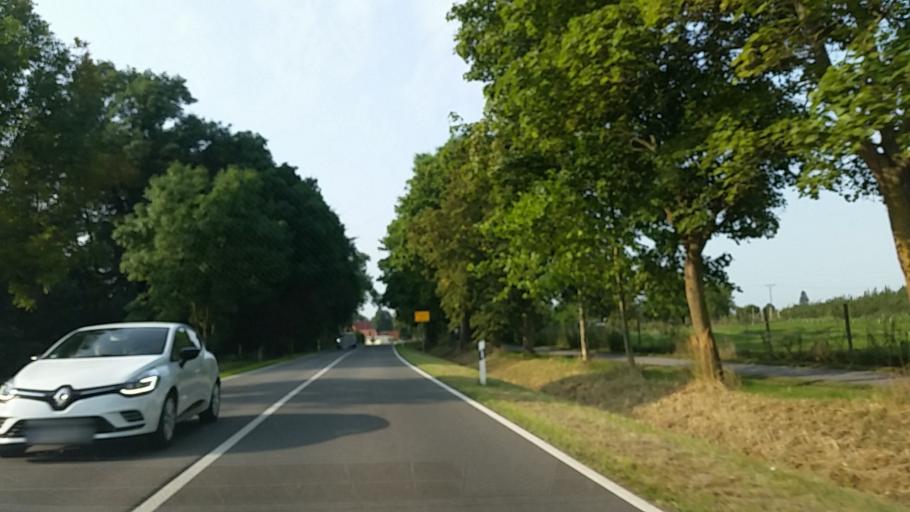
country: DE
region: Mecklenburg-Vorpommern
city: Lubtheen
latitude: 53.3829
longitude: 11.0838
